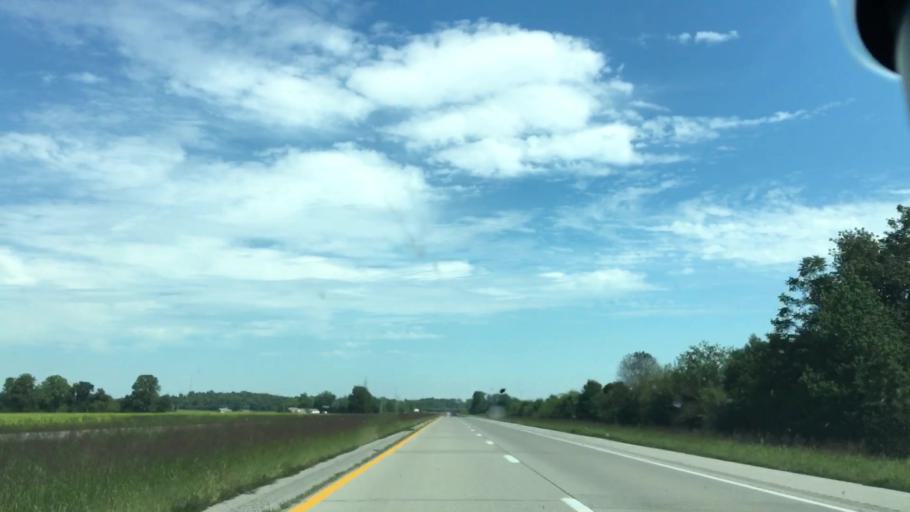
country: US
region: Kentucky
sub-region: Daviess County
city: Owensboro
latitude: 37.7631
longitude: -87.2230
